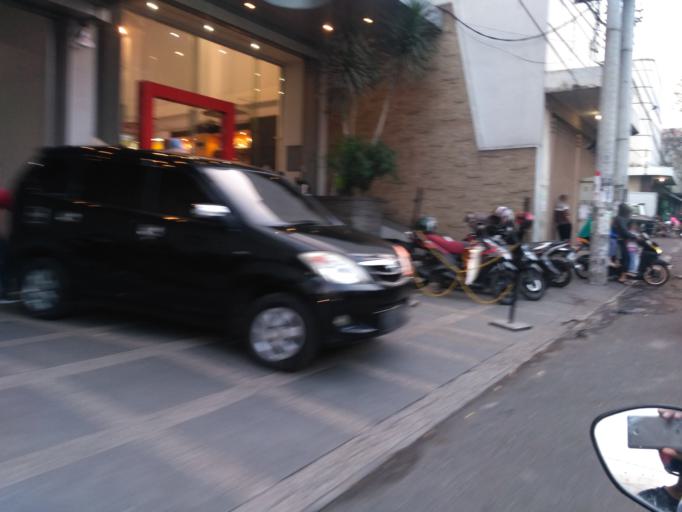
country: ID
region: East Java
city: Malang
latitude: -7.9902
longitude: 112.6345
